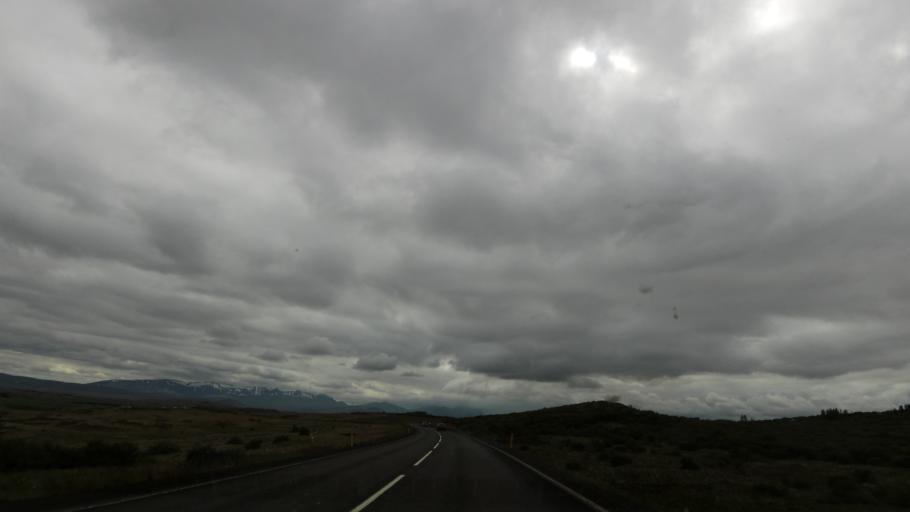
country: IS
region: West
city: Borgarnes
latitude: 64.6912
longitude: -21.6452
